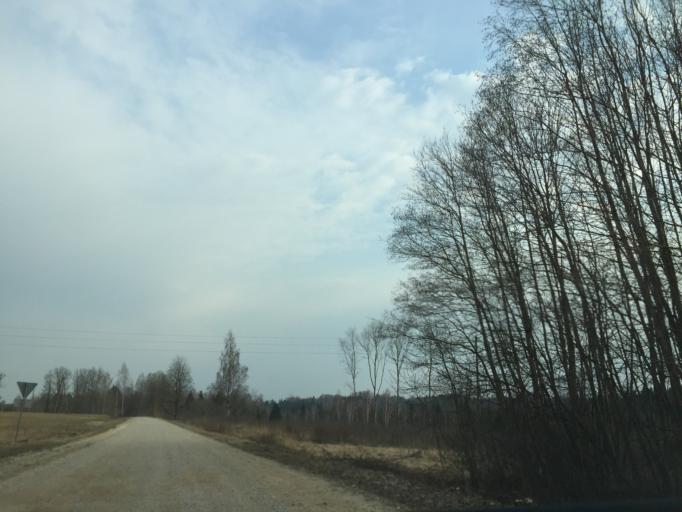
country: LV
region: Raunas
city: Rauna
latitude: 57.1574
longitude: 25.5762
